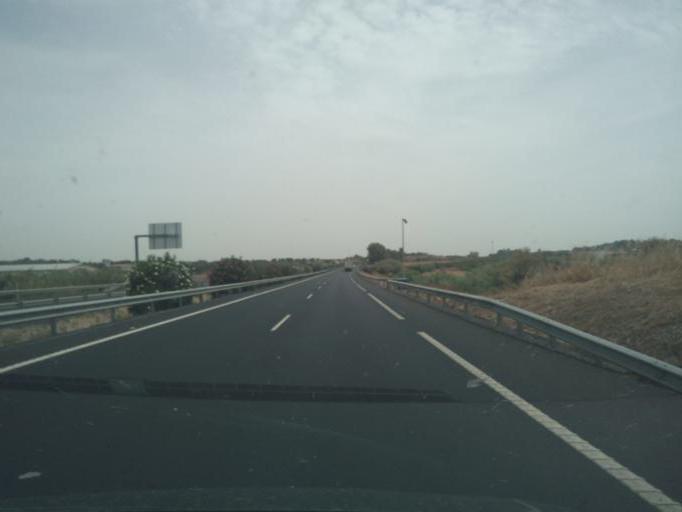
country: ES
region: Andalusia
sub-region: Provincia de Huelva
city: Bollullos par del Condado
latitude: 37.3599
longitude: -6.5248
